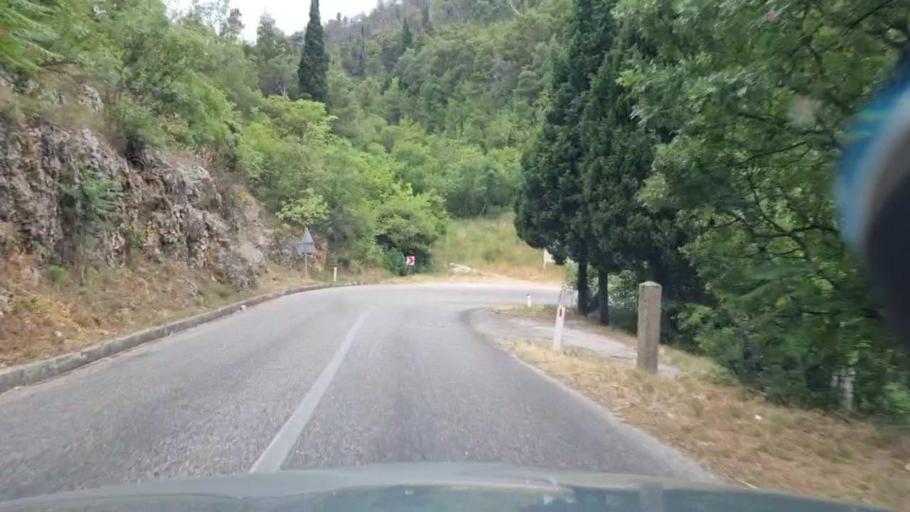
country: BA
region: Federation of Bosnia and Herzegovina
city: Rodoc
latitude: 43.3305
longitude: 17.7966
